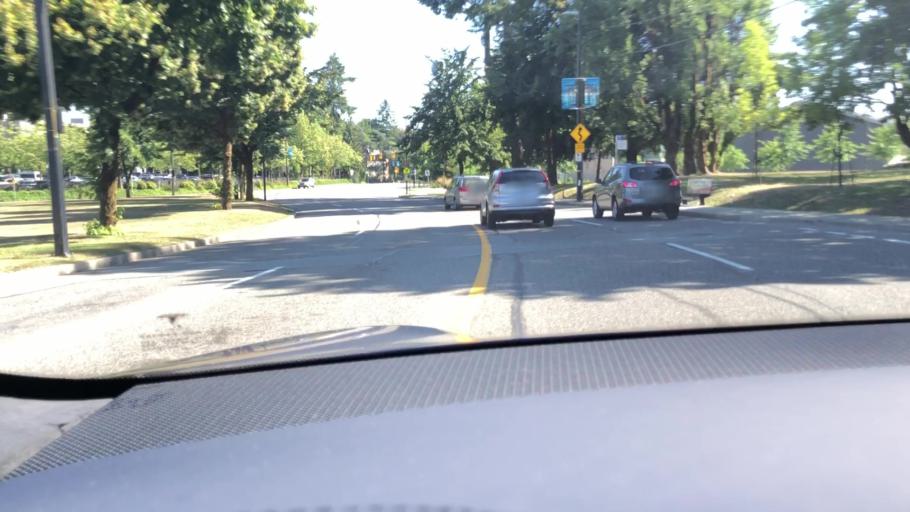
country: CA
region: British Columbia
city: Burnaby
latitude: 49.2453
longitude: -122.9746
